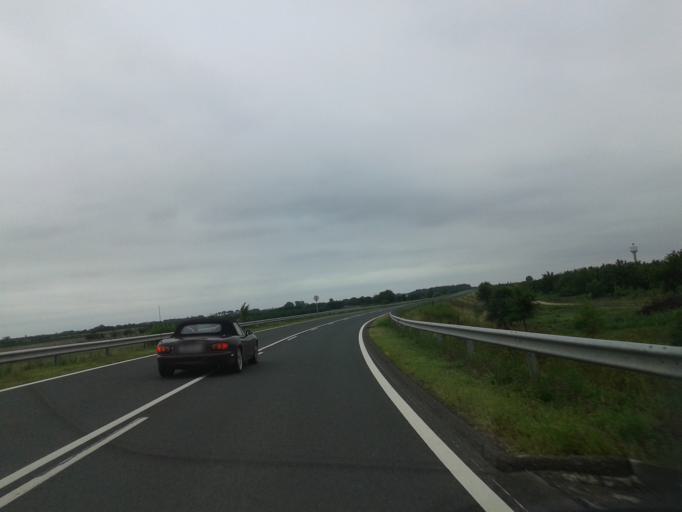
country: HU
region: Bacs-Kiskun
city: Dunavecse
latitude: 46.9321
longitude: 18.9889
